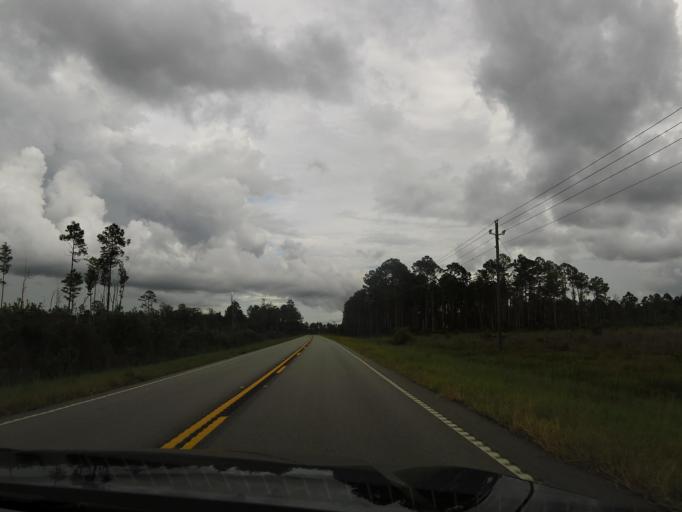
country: US
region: Florida
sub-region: Baker County
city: Macclenny
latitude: 30.5242
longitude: -82.1647
